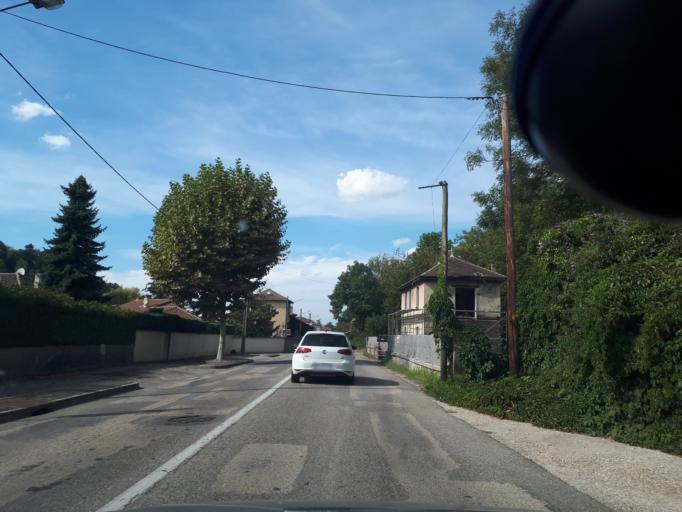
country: FR
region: Rhone-Alpes
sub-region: Departement de l'Isere
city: Bourgoin-Jallieu
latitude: 45.5771
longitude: 5.2759
